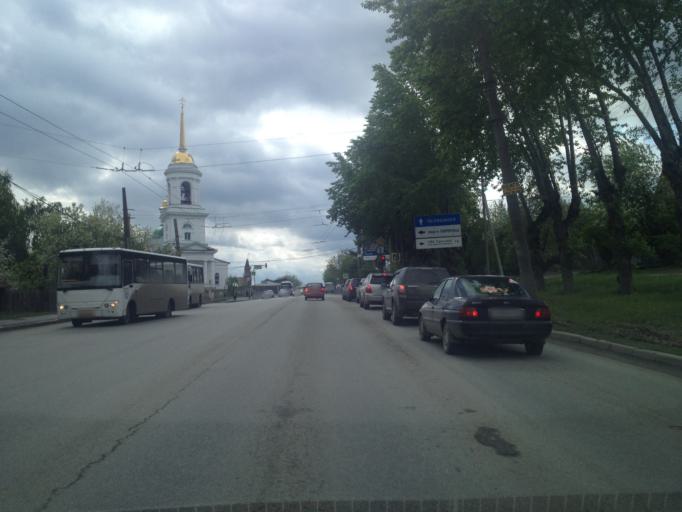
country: RU
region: Sverdlovsk
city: Istok
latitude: 56.7469
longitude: 60.6864
